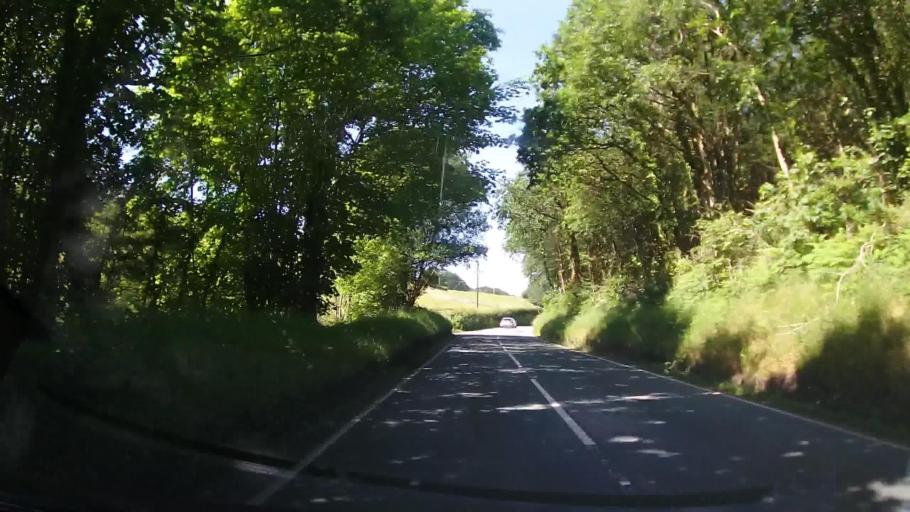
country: GB
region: Wales
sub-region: Sir Powys
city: Machynlleth
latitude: 52.5910
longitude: -3.8807
